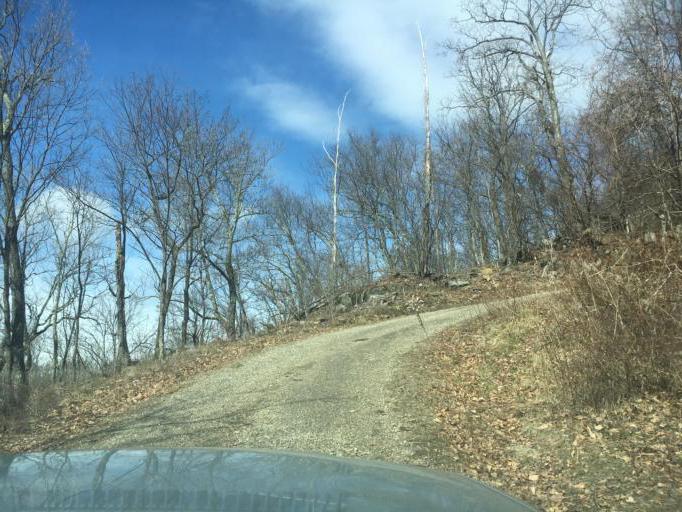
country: US
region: North Carolina
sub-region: Haywood County
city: Canton
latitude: 35.4708
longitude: -82.8372
